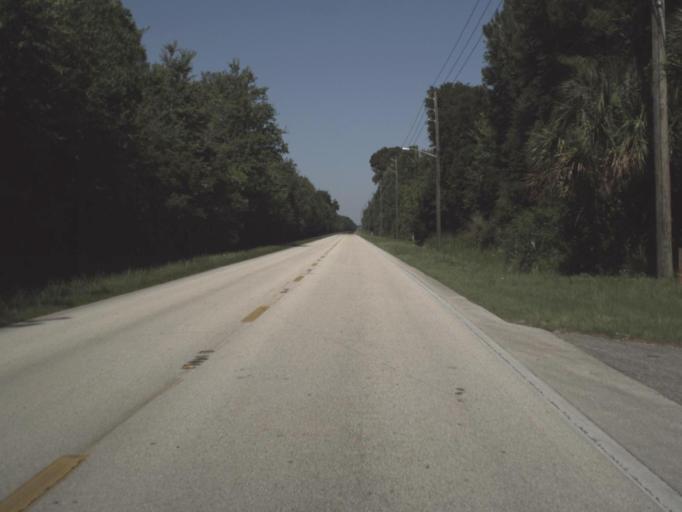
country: US
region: Florida
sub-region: Duval County
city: Baldwin
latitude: 30.3091
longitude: -81.8986
